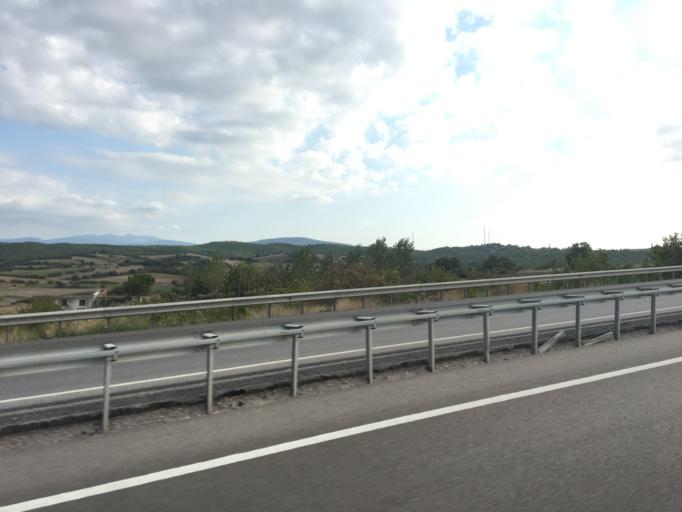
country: TR
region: Bursa
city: Tatkavakli
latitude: 40.0297
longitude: 28.2696
